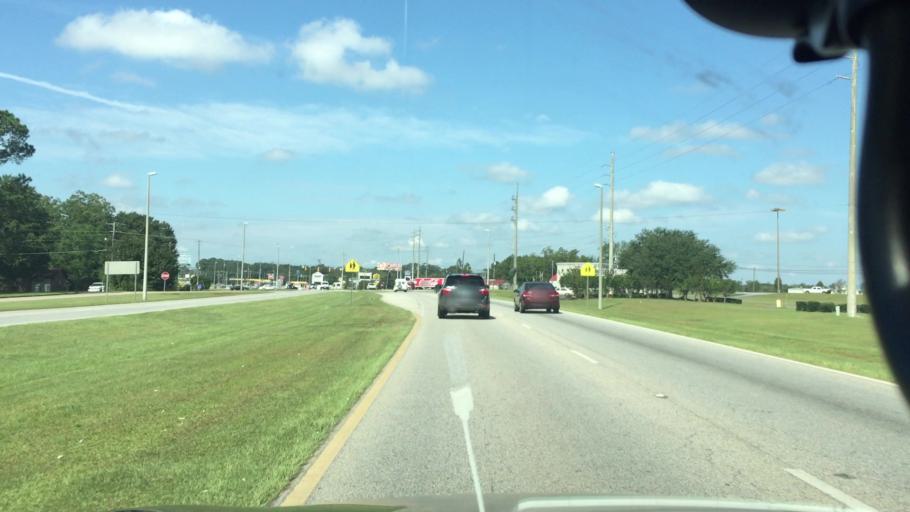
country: US
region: Alabama
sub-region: Coffee County
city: Enterprise
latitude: 31.3348
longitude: -85.8511
